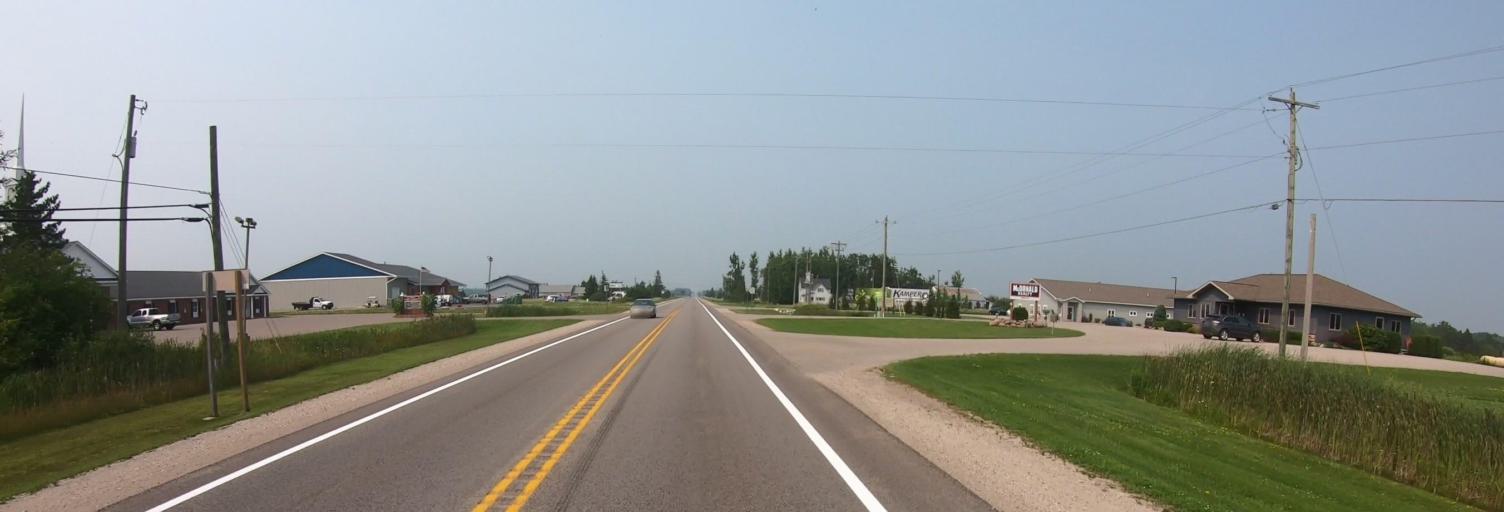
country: US
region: Michigan
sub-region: Chippewa County
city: Sault Ste. Marie
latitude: 46.1615
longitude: -84.3635
